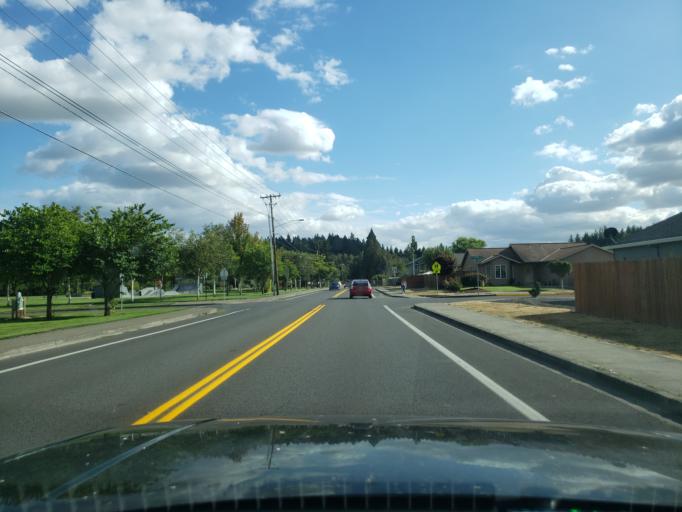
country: US
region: Oregon
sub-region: Yamhill County
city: McMinnville
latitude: 45.1989
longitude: -123.2191
